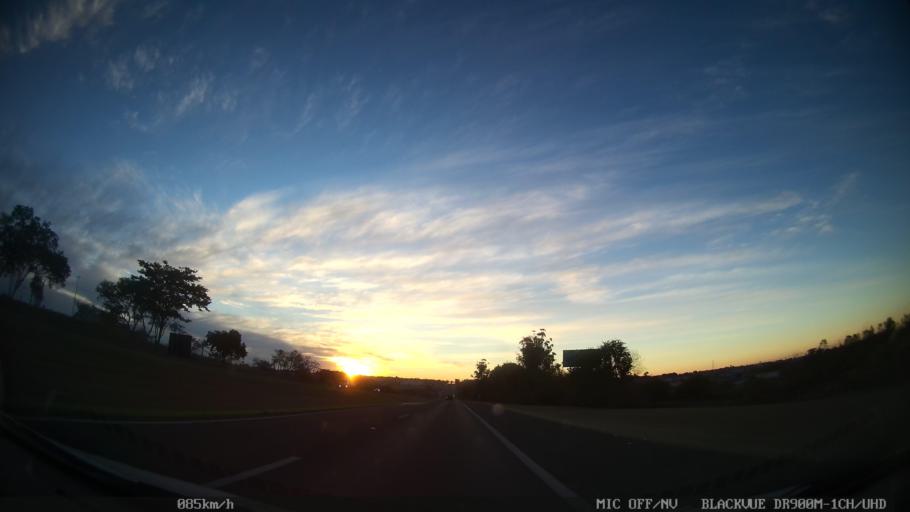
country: BR
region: Sao Paulo
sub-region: Catanduva
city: Catanduva
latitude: -21.1649
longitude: -48.9799
